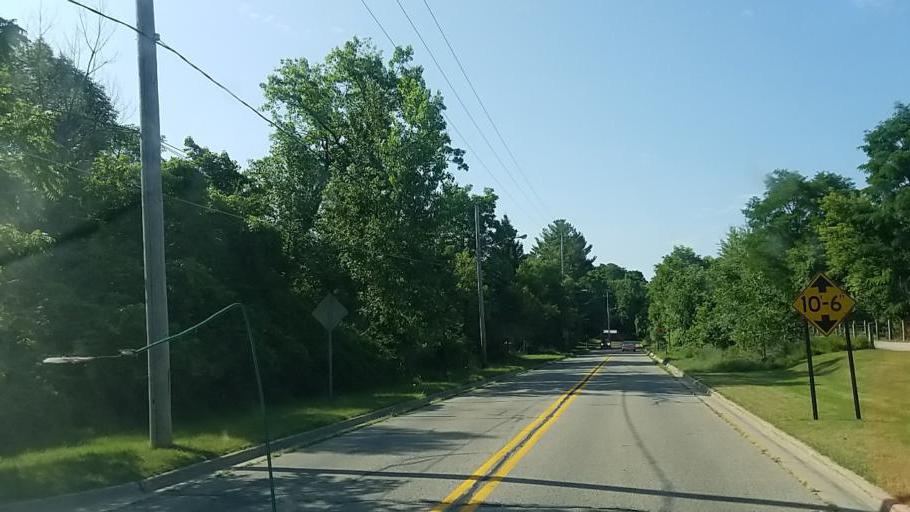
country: US
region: Michigan
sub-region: Muskegon County
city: Whitehall
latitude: 43.4054
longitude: -86.3491
